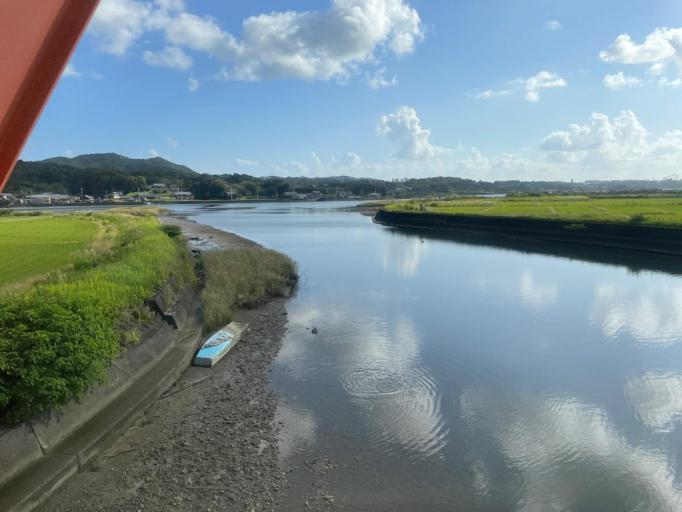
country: JP
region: Mie
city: Toba
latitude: 34.3642
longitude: 136.8118
